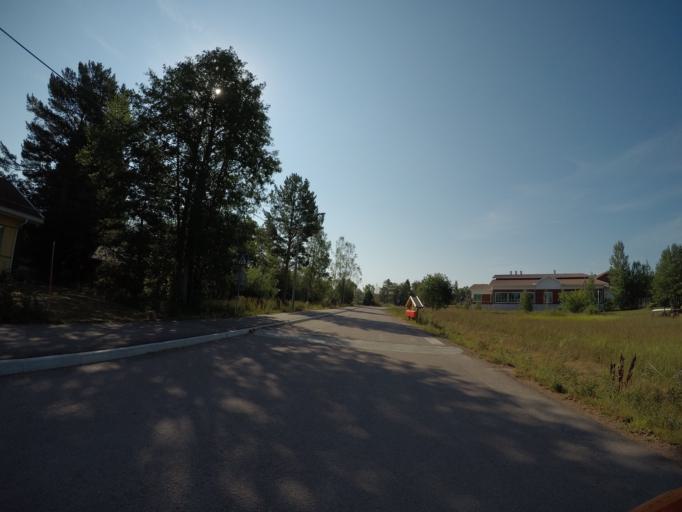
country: AX
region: Alands landsbygd
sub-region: Finstroem
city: Finstroem
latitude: 60.2259
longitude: 19.9799
